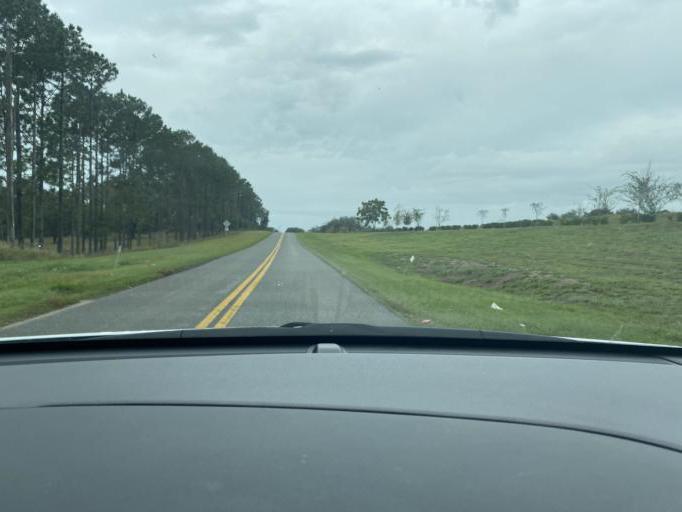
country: US
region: Florida
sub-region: Lake County
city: Clermont
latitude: 28.6021
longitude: -81.8026
